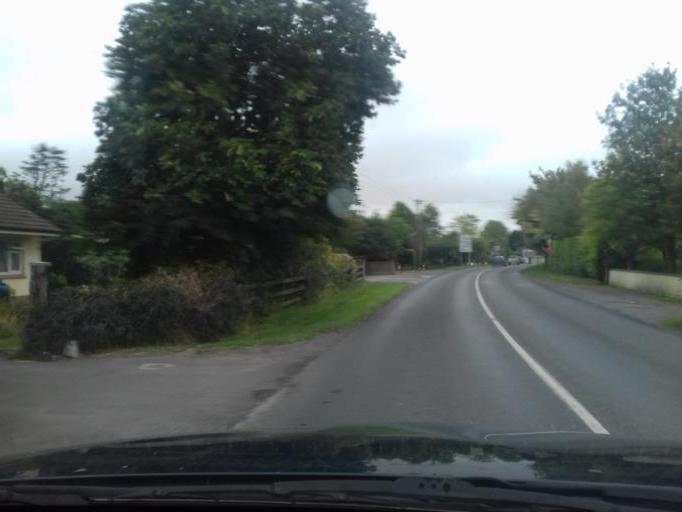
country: IE
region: Leinster
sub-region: County Carlow
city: Bagenalstown
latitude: 52.6924
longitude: -6.9608
